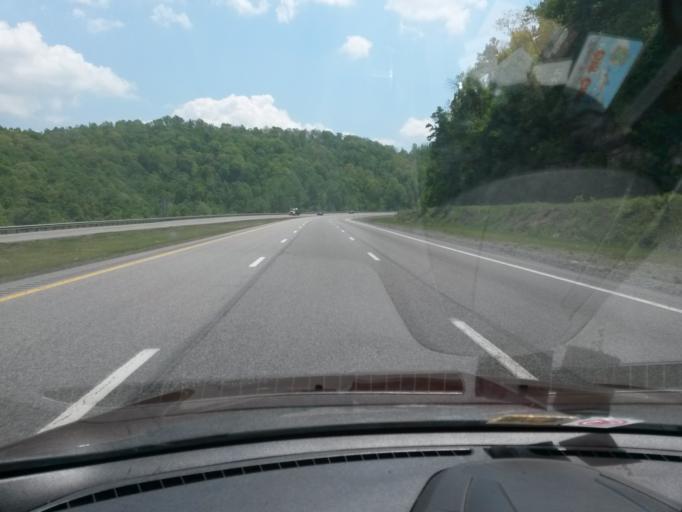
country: US
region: West Virginia
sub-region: Braxton County
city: Sutton
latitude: 38.5388
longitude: -80.7233
